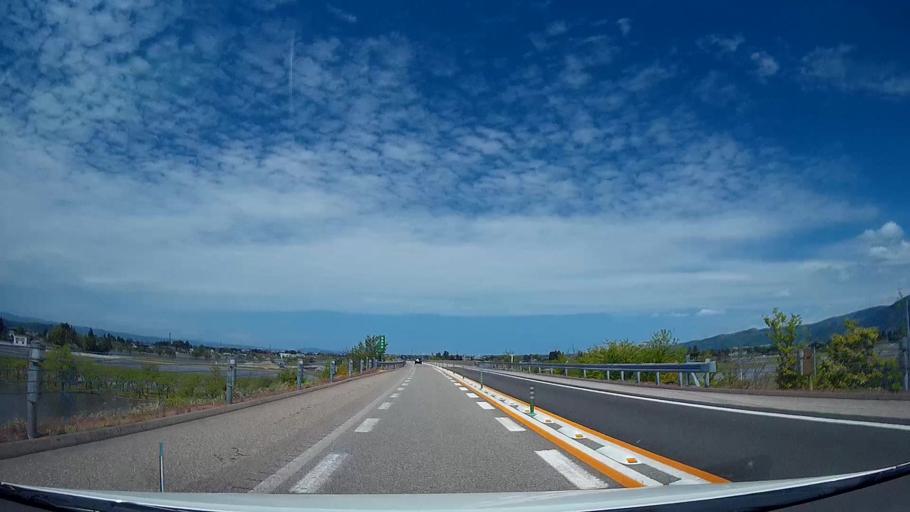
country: JP
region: Toyama
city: Nanto-shi
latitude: 36.5467
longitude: 136.8975
